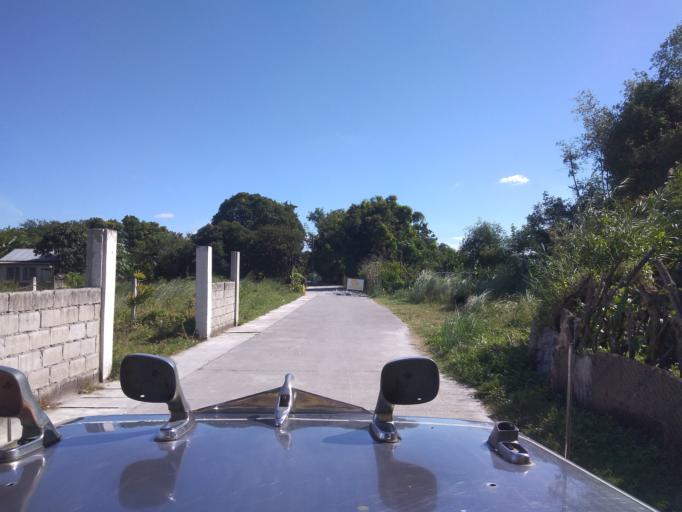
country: PH
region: Central Luzon
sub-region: Province of Pampanga
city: Bacolor
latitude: 15.0255
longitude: 120.6340
